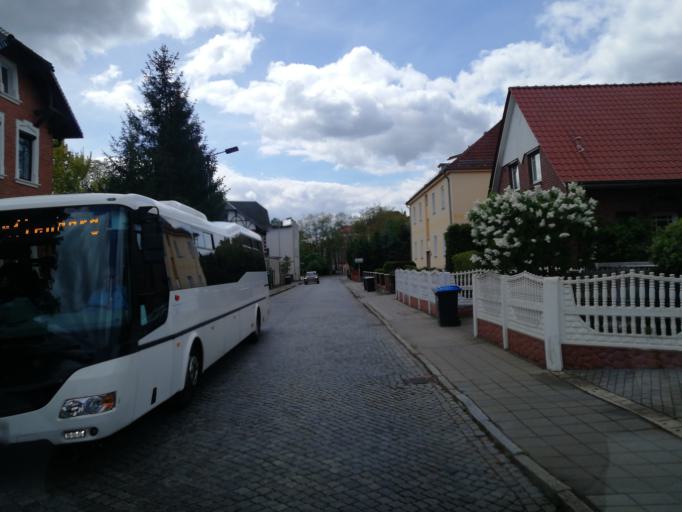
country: DE
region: Brandenburg
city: Lauchhammer
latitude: 51.4991
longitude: 13.7943
